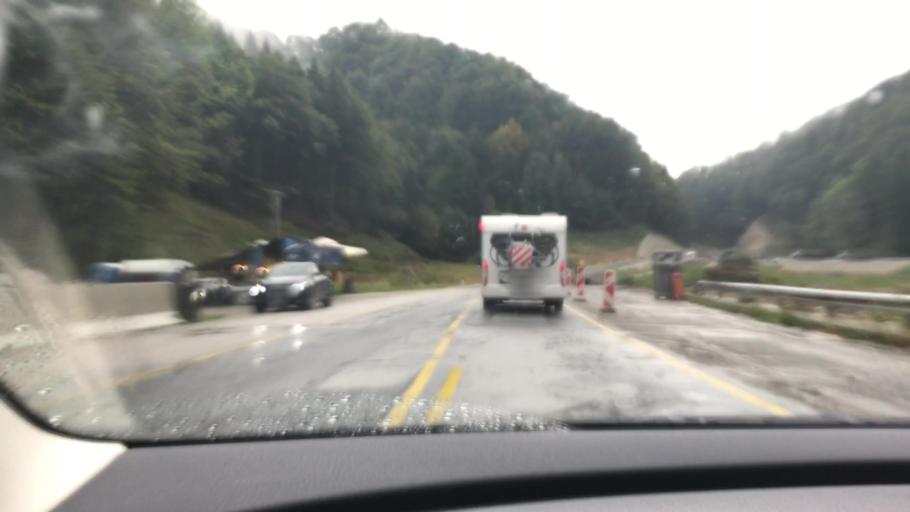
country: SI
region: Zetale
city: Zetale
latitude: 46.2861
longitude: 15.8590
